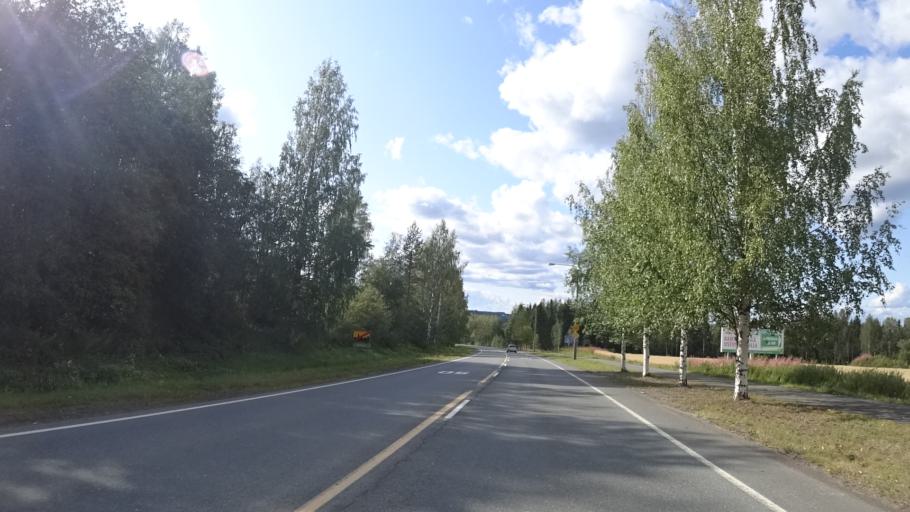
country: FI
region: North Karelia
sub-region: Keski-Karjala
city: Tohmajaervi
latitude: 62.2274
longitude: 30.3296
